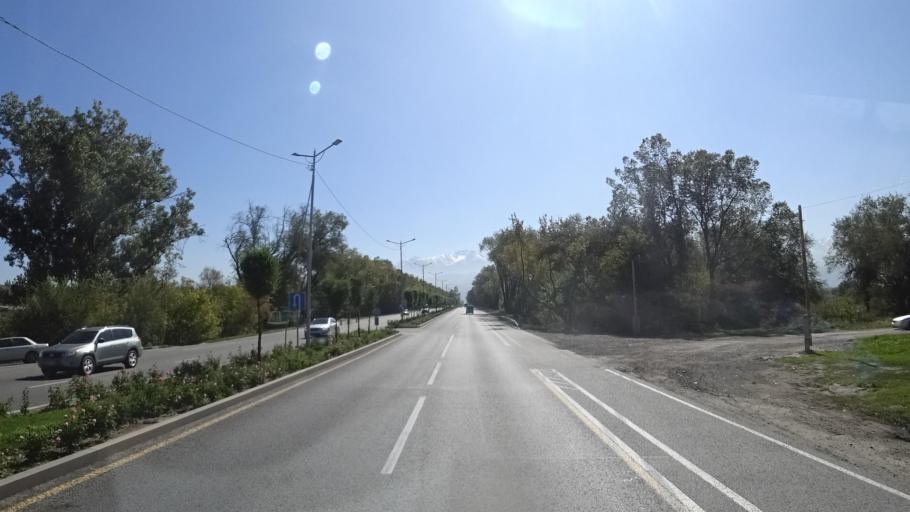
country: KZ
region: Almaty Oblysy
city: Pervomayskiy
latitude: 43.3277
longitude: 77.0133
